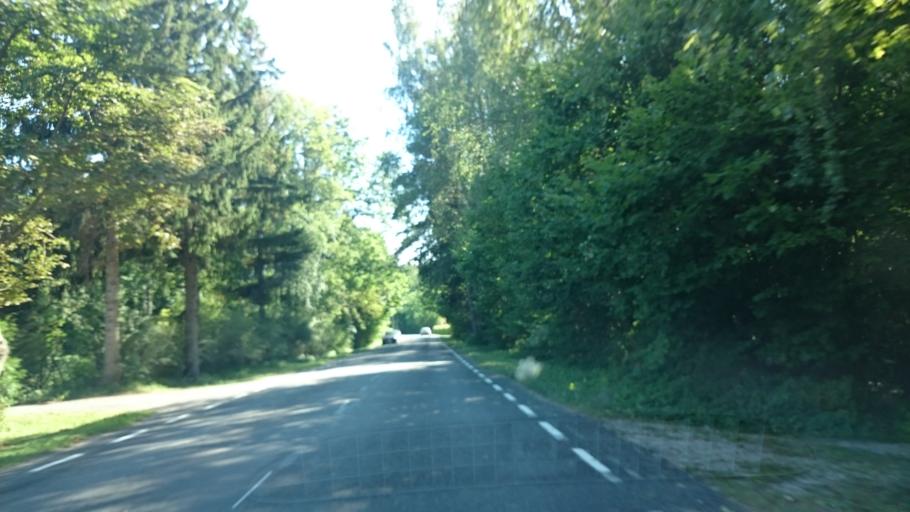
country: EE
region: Saare
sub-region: Kuressaare linn
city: Kuressaare
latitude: 58.5768
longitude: 22.6866
